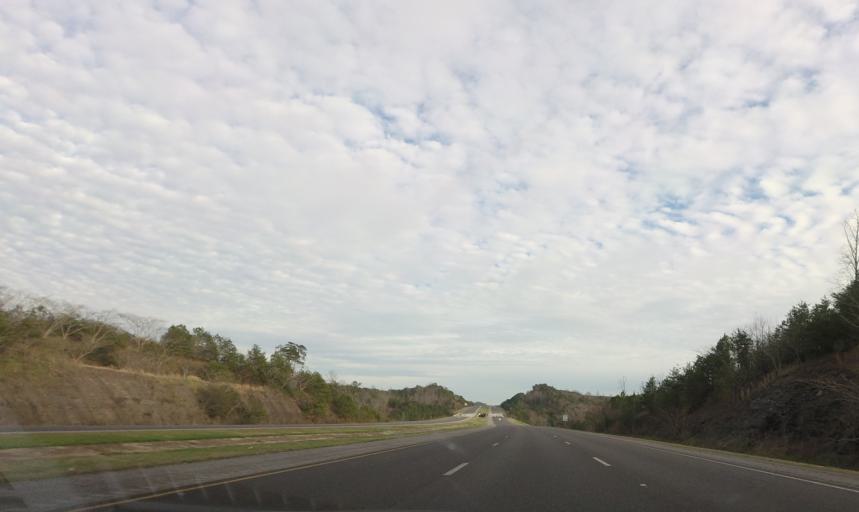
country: US
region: Alabama
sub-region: Jefferson County
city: Brookside
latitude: 33.6049
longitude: -86.9197
